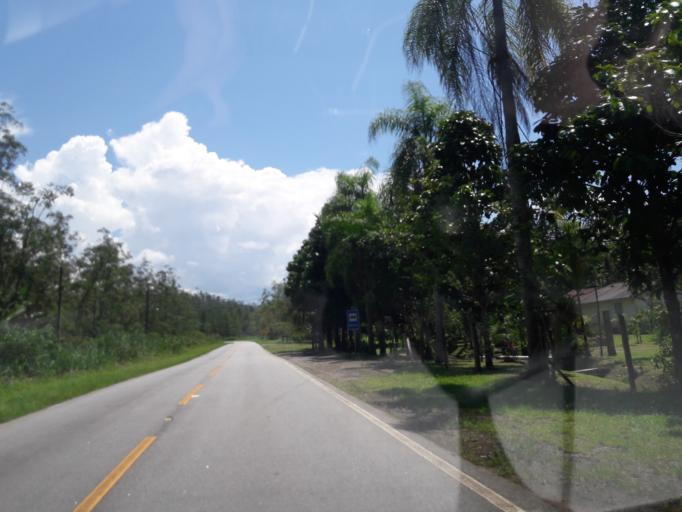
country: BR
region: Parana
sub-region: Antonina
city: Antonina
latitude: -25.5251
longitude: -48.7794
